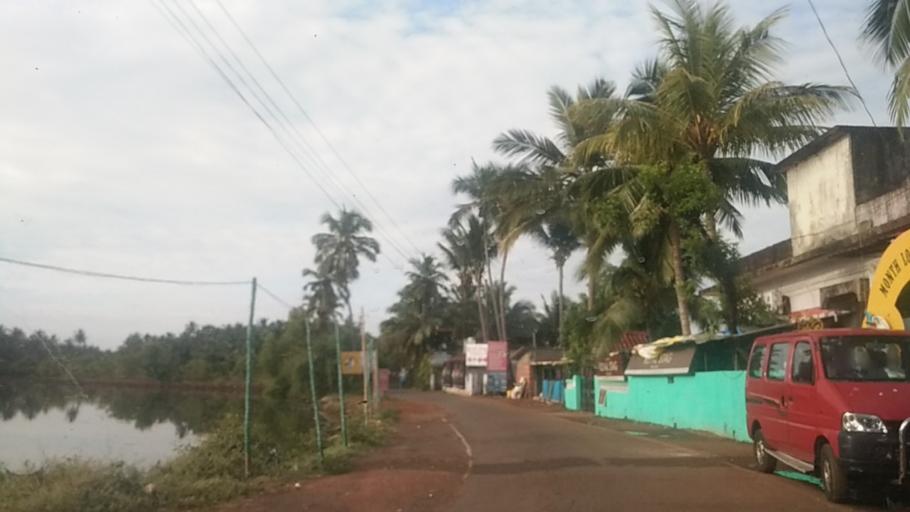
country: IN
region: Goa
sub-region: South Goa
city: Cavelossim
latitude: 15.1809
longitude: 73.9642
